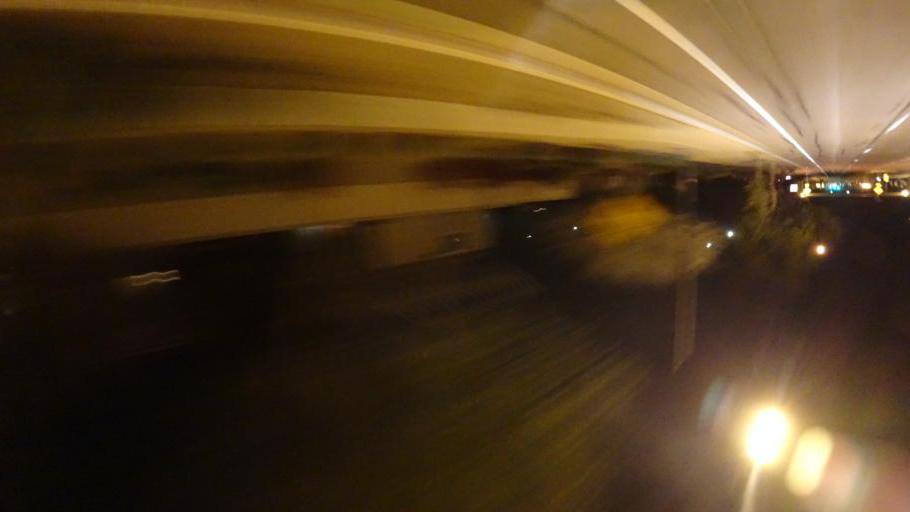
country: US
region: Arizona
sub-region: Maricopa County
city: Gilbert
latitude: 33.3268
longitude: -111.7041
